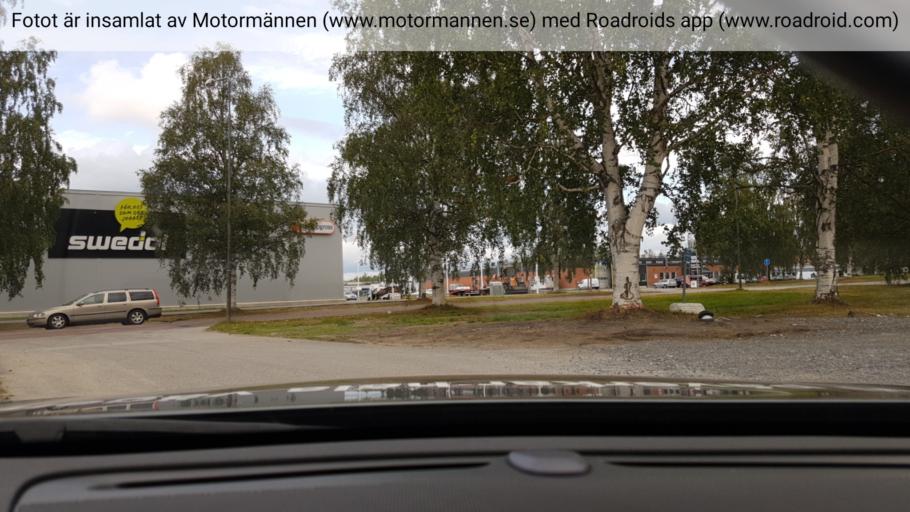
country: SE
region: Vaesterbotten
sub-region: Umea Kommun
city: Umea
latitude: 63.8401
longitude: 20.2390
